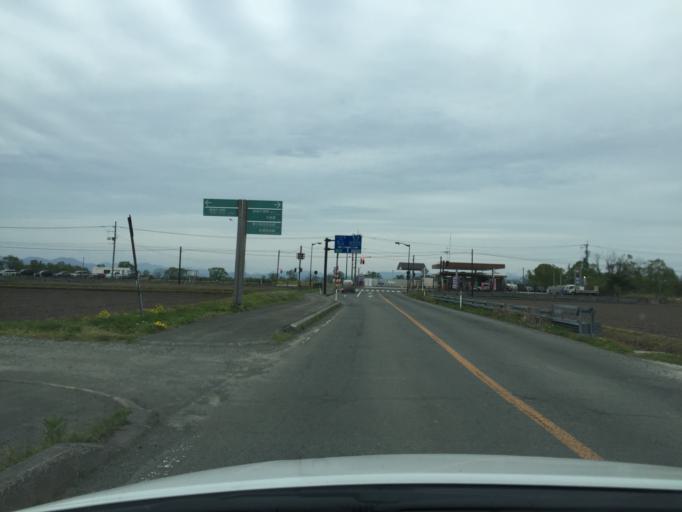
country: JP
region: Fukushima
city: Inawashiro
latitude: 37.5377
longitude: 140.0777
